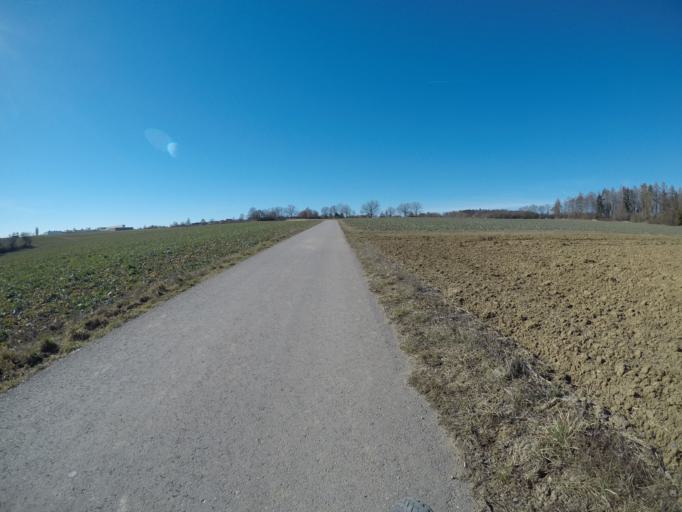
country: DE
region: Baden-Wuerttemberg
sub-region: Regierungsbezirk Stuttgart
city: Herrenberg
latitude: 48.5667
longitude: 8.8587
